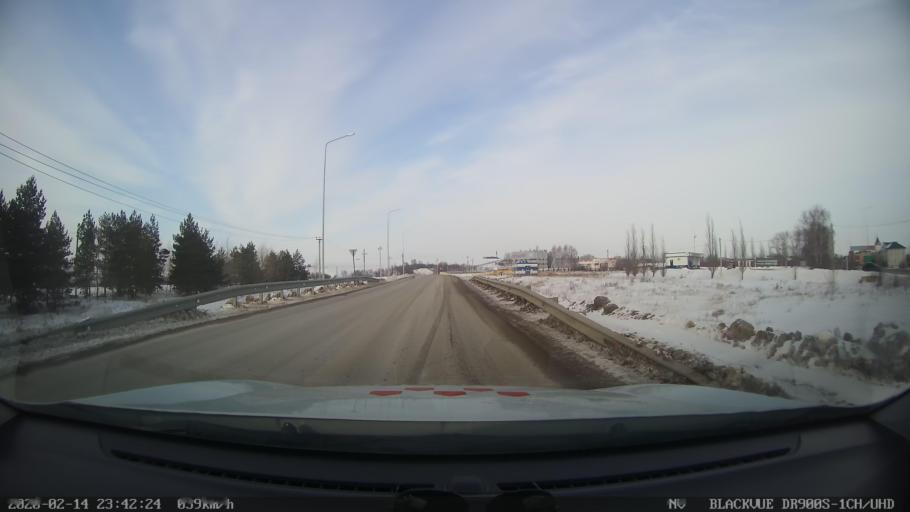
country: RU
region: Tatarstan
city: Kuybyshevskiy Zaton
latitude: 55.1914
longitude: 49.2471
